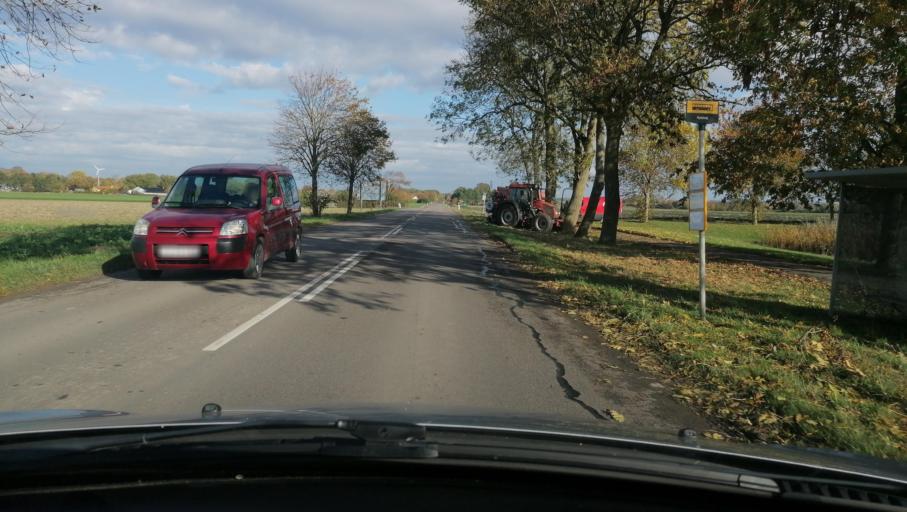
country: DK
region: Zealand
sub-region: Odsherred Kommune
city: Horve
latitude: 55.7932
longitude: 11.4600
